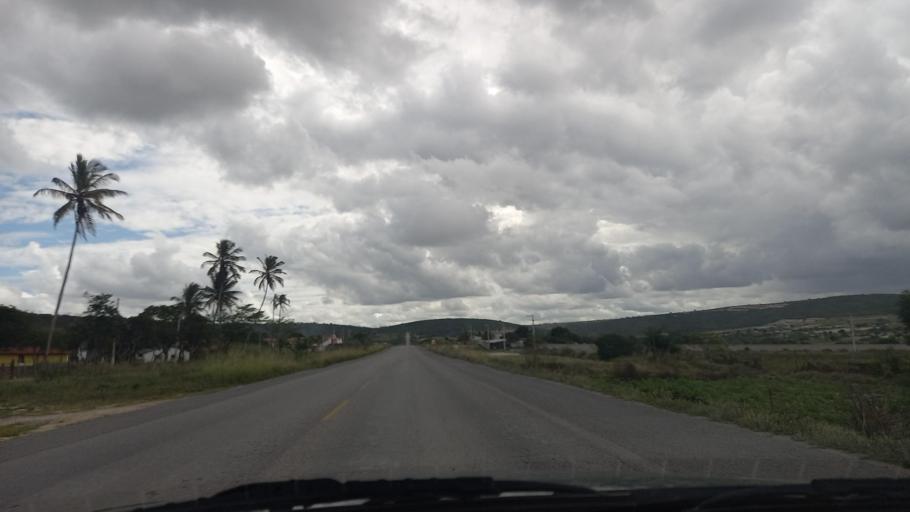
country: BR
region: Pernambuco
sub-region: Lajedo
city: Lajedo
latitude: -8.6687
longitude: -36.3761
